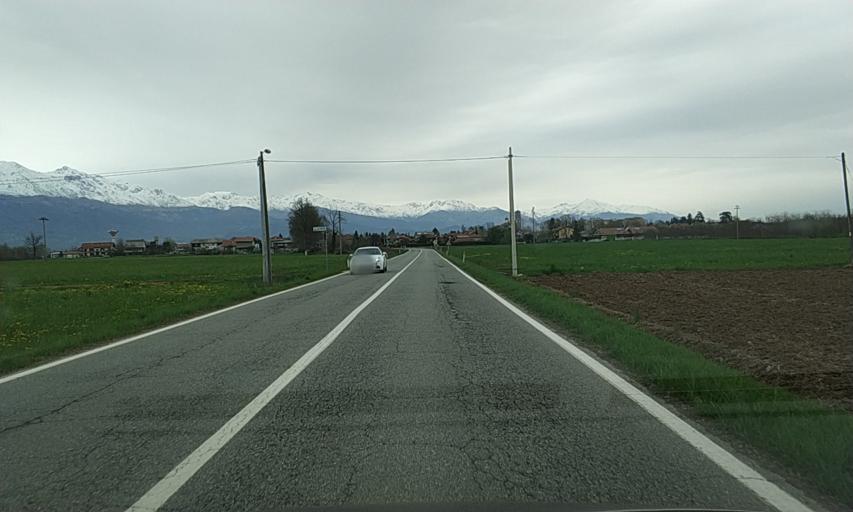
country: IT
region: Piedmont
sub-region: Provincia di Torino
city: Favria
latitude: 45.3231
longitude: 7.6847
